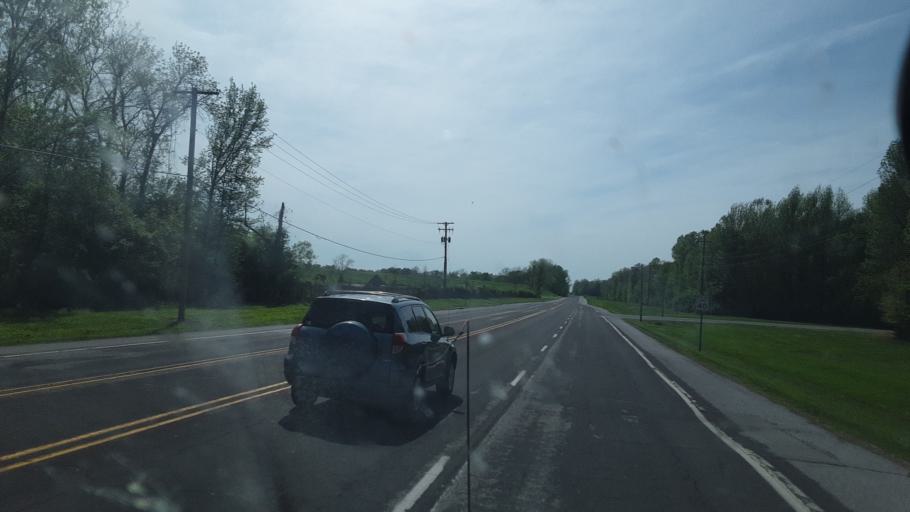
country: US
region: Illinois
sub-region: Jackson County
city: Carbondale
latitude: 37.7005
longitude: -89.2205
